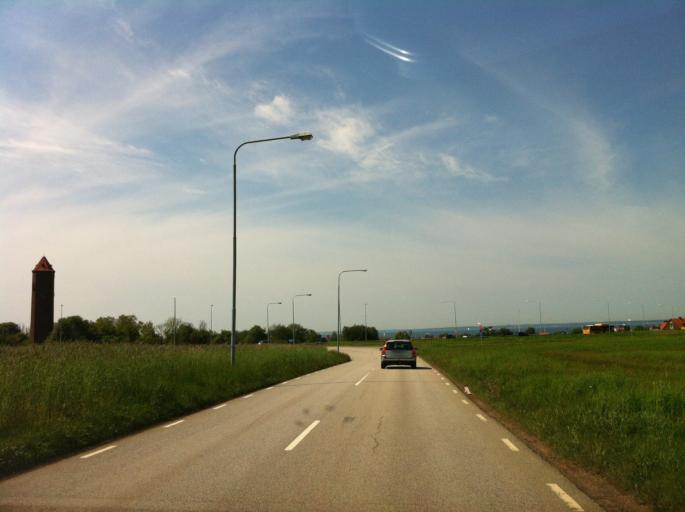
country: SE
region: Skane
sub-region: Helsingborg
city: Glumslov
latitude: 55.9290
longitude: 12.8415
